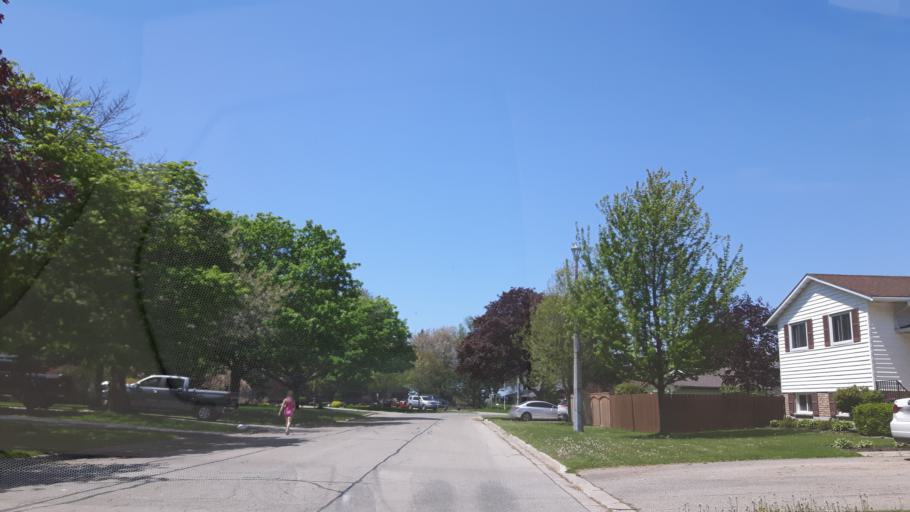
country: CA
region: Ontario
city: Goderich
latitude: 43.7304
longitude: -81.7190
